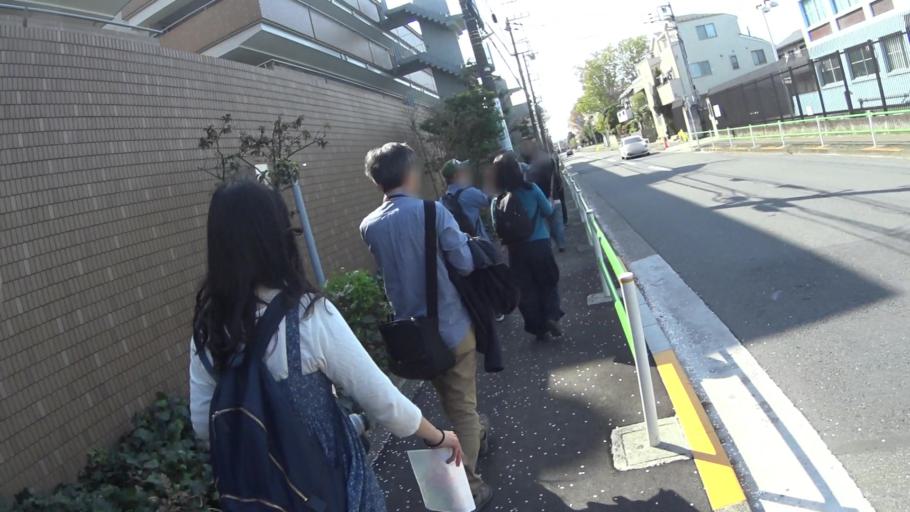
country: JP
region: Tokyo
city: Kokubunji
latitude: 35.7111
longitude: 139.4918
